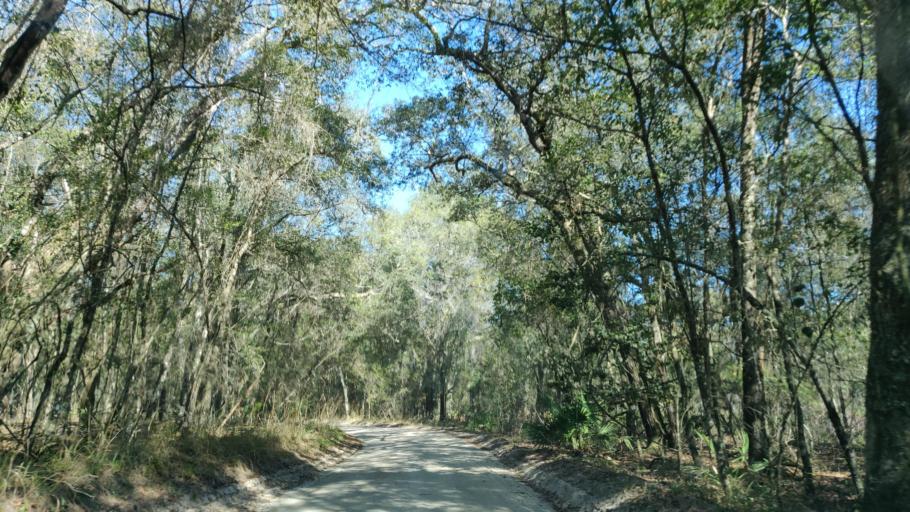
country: US
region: Florida
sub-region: Clay County
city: Middleburg
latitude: 30.1537
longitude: -81.9323
